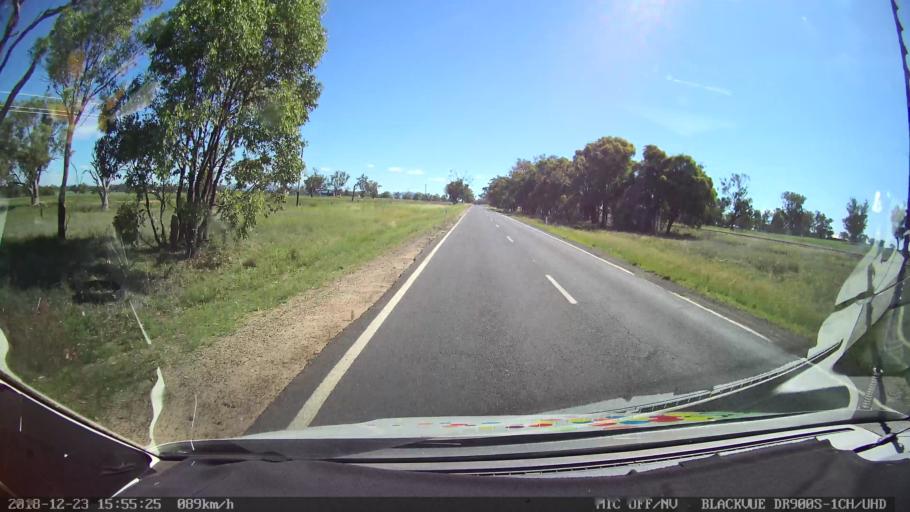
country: AU
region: New South Wales
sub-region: Tamworth Municipality
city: Phillip
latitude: -31.1553
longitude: 150.8686
